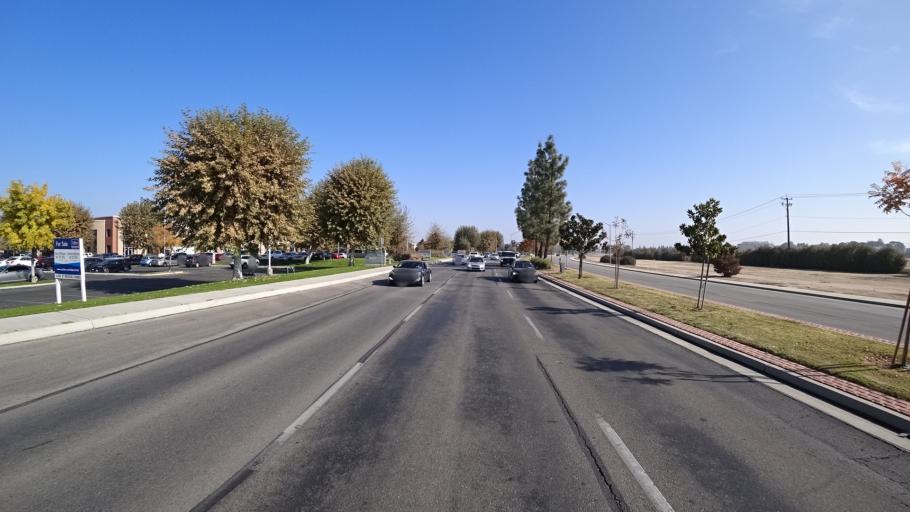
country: US
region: California
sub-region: Kern County
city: Greenacres
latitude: 35.3542
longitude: -119.1121
